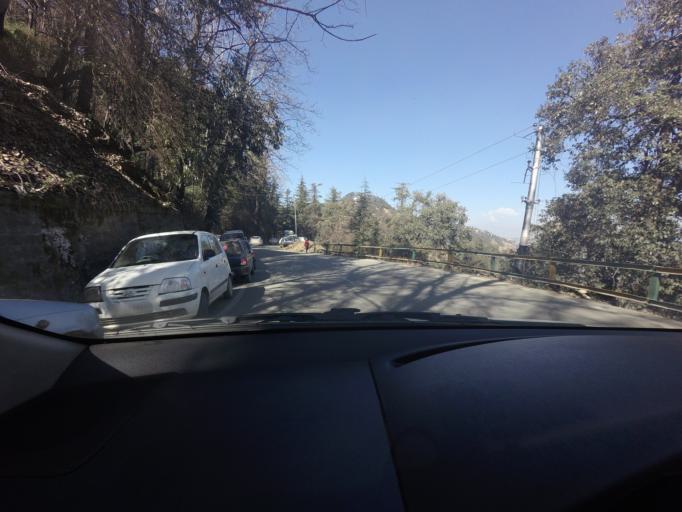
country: IN
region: Himachal Pradesh
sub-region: Shimla
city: Shimla
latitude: 31.1076
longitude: 77.1834
